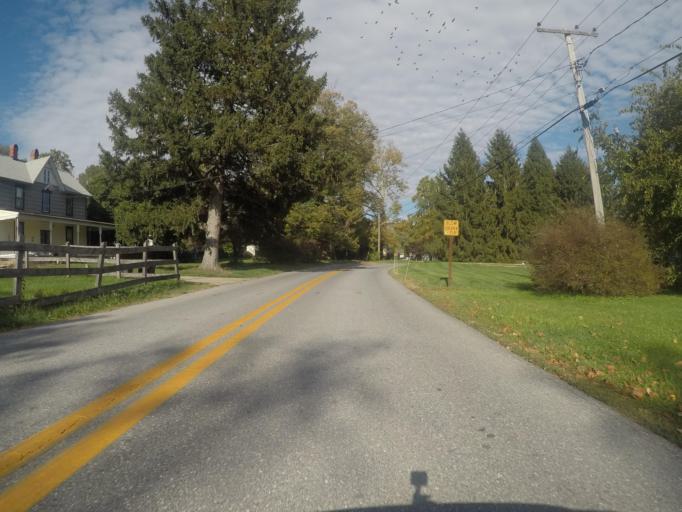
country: US
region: Maryland
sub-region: Carroll County
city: Hampstead
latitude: 39.5636
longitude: -76.8345
